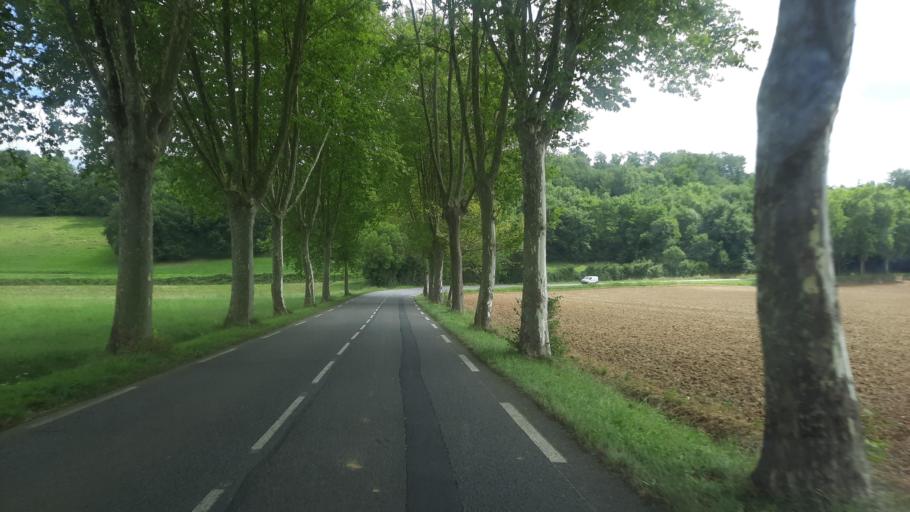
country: FR
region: Midi-Pyrenees
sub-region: Departement des Hautes-Pyrenees
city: Trie-sur-Baise
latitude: 43.3203
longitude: 0.3797
